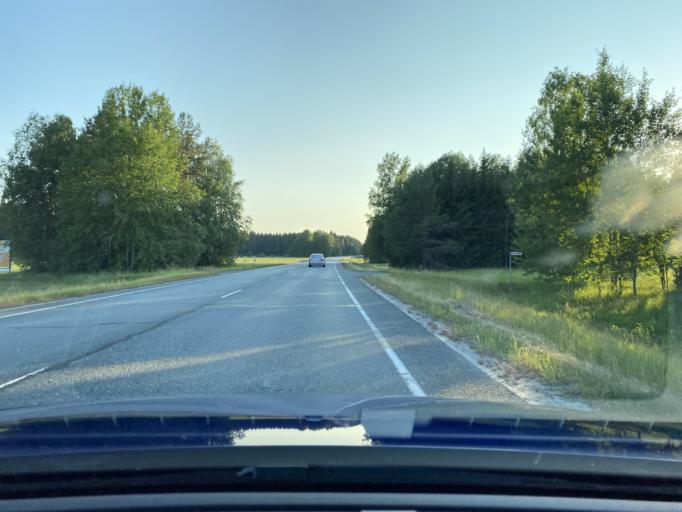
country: FI
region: Haeme
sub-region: Forssa
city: Tammela
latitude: 60.8259
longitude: 23.7957
